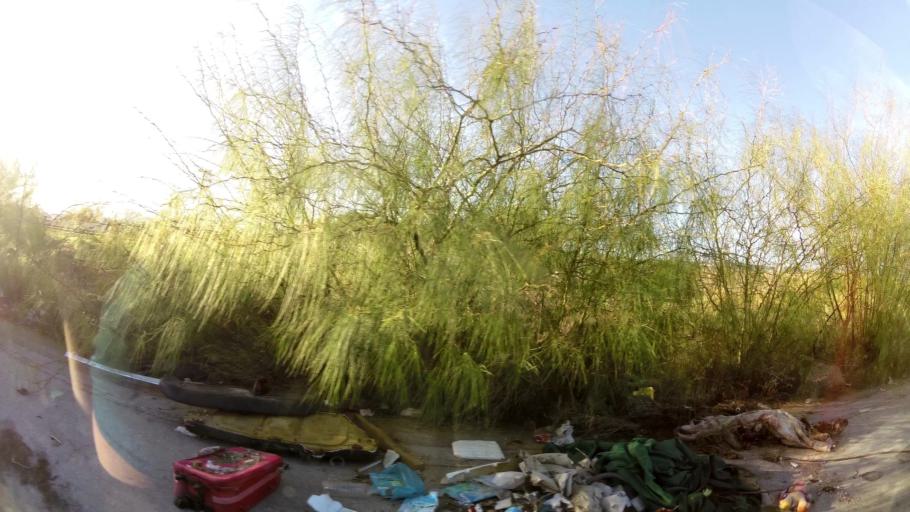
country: GR
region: Attica
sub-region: Nomarchia Athinas
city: Skaramangas
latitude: 38.0356
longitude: 23.6258
